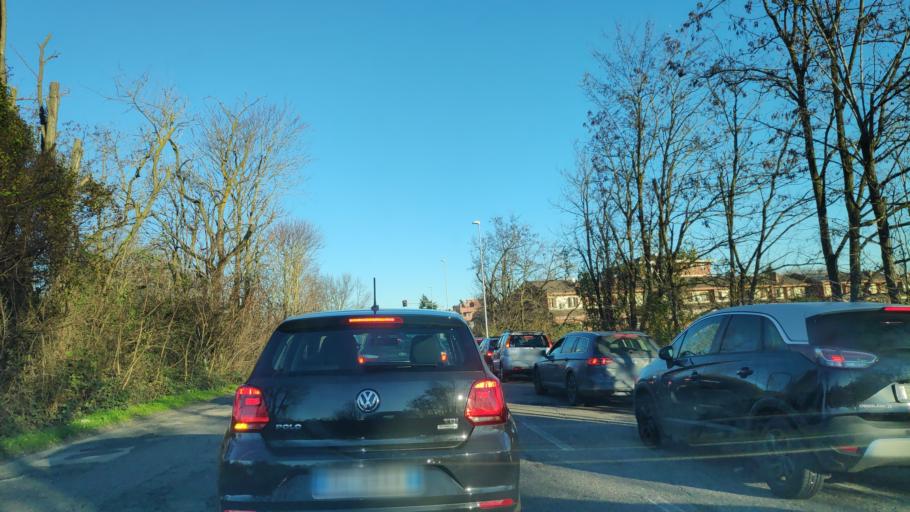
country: IT
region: Lombardy
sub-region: Citta metropolitana di Milano
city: Fizzonasco
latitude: 45.3662
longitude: 9.1896
